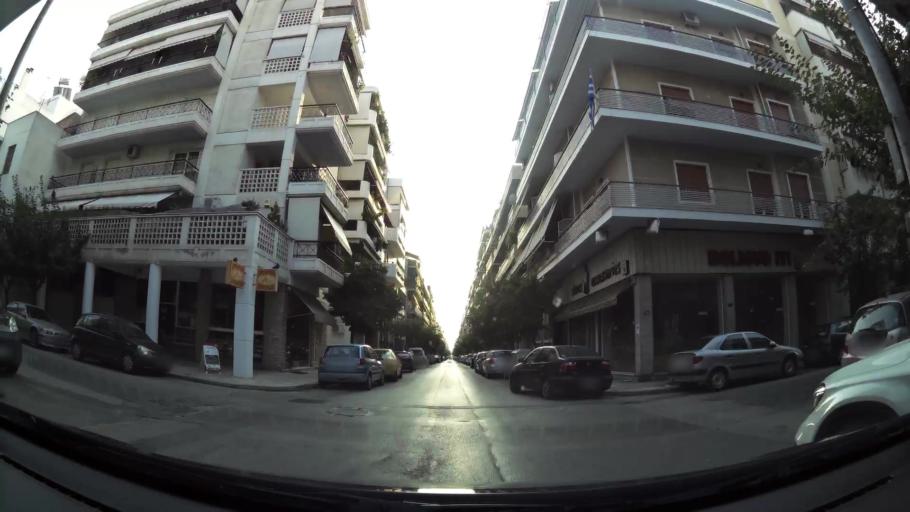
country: GR
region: Attica
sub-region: Nomarchia Athinas
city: Kallithea
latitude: 37.9622
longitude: 23.7057
